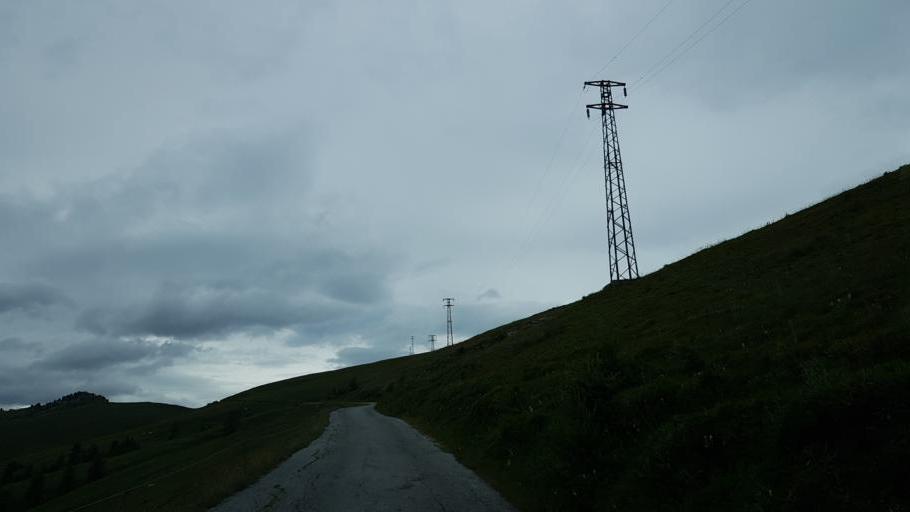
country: IT
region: Piedmont
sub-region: Provincia di Cuneo
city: Serre
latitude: 44.5387
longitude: 7.1182
